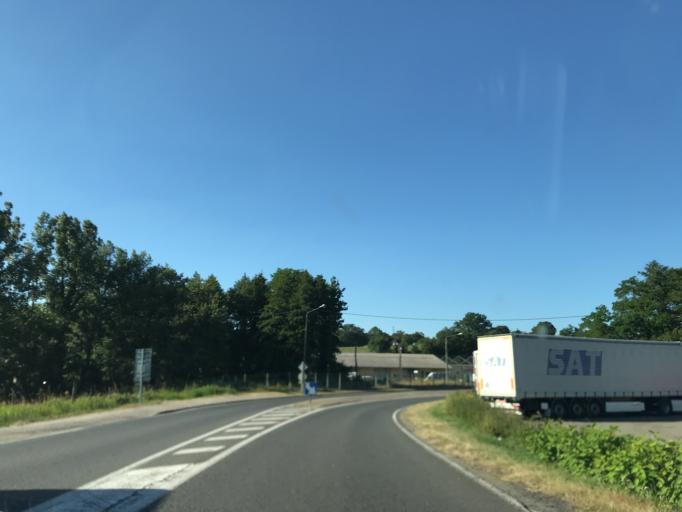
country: FR
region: Auvergne
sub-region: Departement du Puy-de-Dome
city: Peschadoires
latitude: 45.8634
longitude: 3.5047
